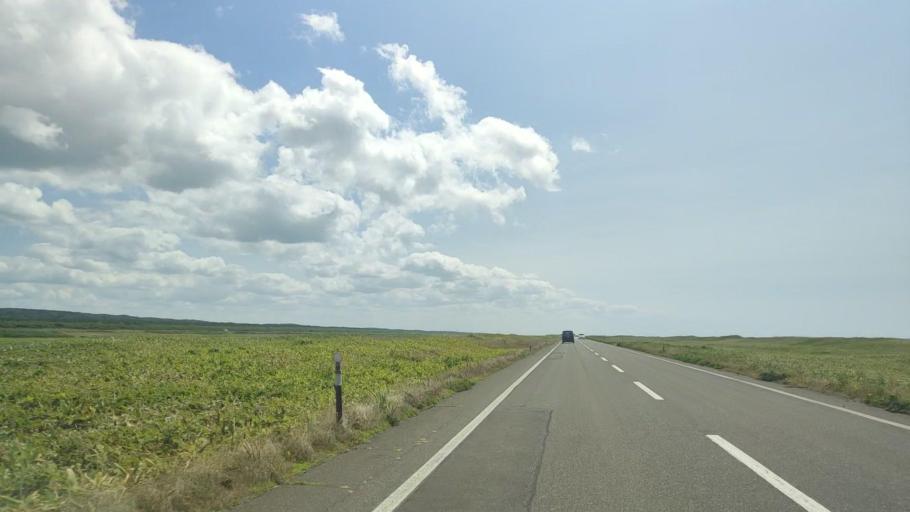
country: JP
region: Hokkaido
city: Wakkanai
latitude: 45.1143
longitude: 141.6130
